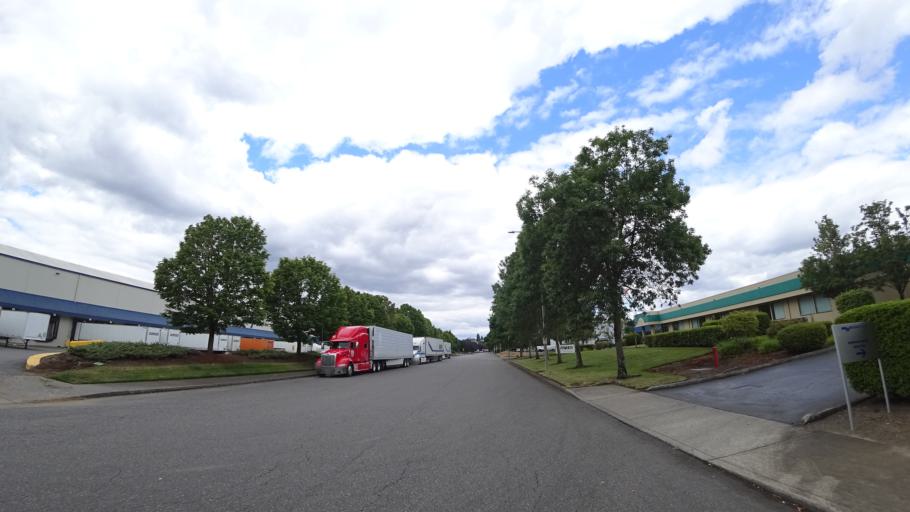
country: US
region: Oregon
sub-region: Multnomah County
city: Portland
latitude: 45.5675
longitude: -122.7039
